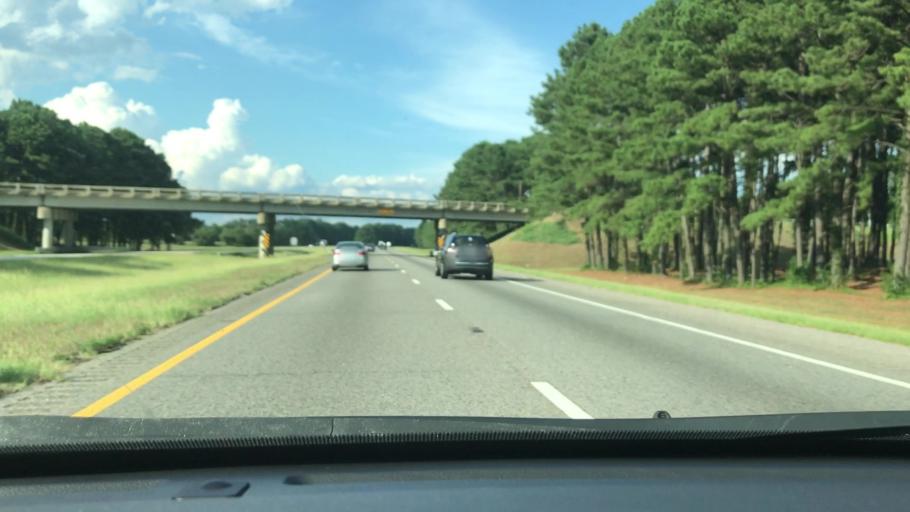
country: US
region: South Carolina
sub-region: Dillon County
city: Dillon
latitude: 34.4182
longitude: -79.4131
